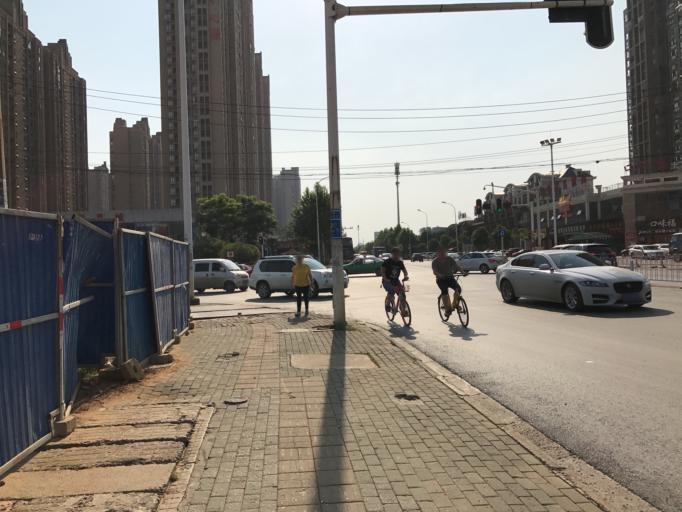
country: CN
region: Hubei
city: Shizishan
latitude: 30.4840
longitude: 114.3208
